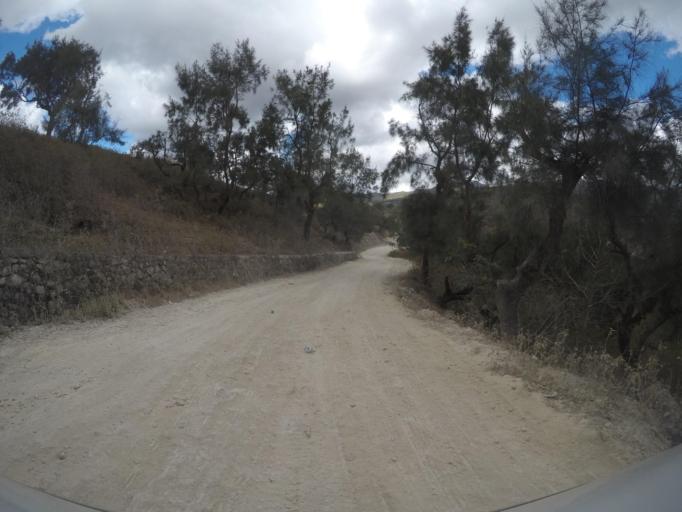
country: TL
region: Baucau
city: Baucau
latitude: -8.4996
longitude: 126.6773
